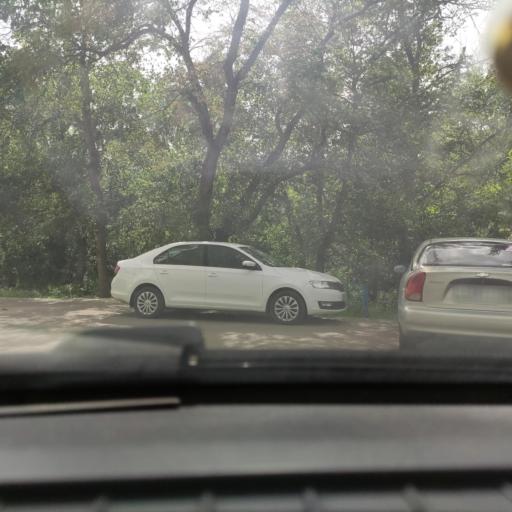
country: RU
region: Voronezj
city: Pridonskoy
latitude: 51.6267
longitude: 39.0673
